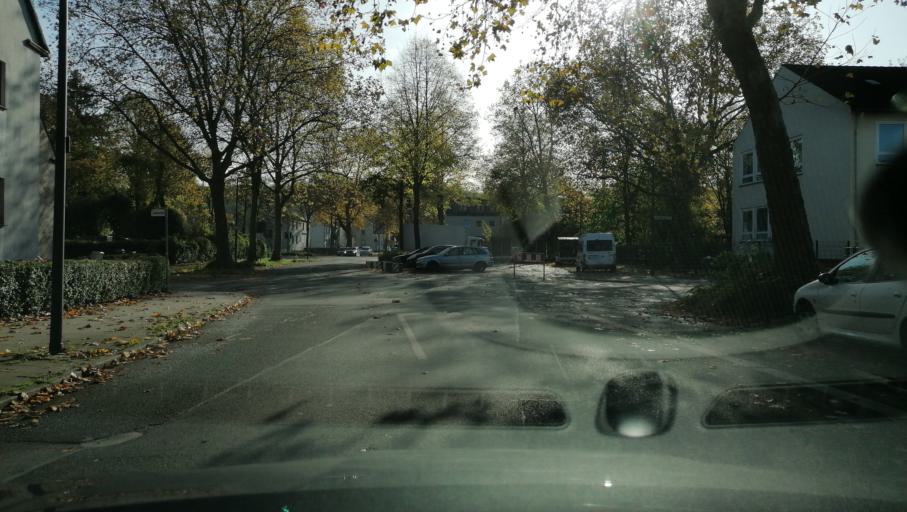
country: DE
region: North Rhine-Westphalia
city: Herten
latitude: 51.5783
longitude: 7.1508
